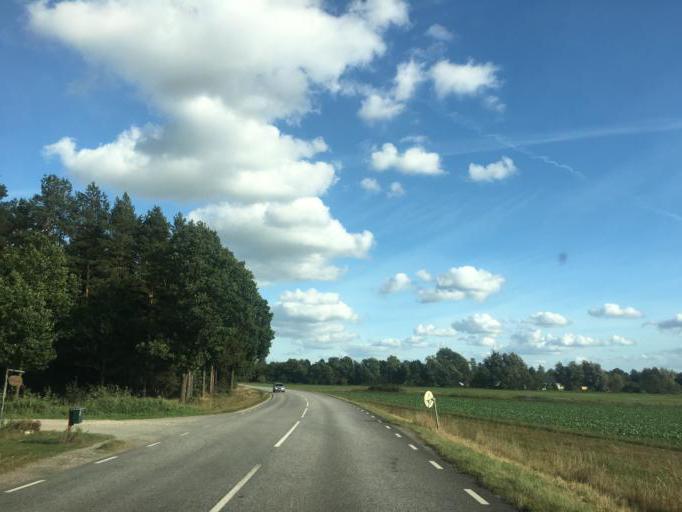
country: SE
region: Skane
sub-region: Hoors Kommun
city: Loberod
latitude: 55.7335
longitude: 13.4562
